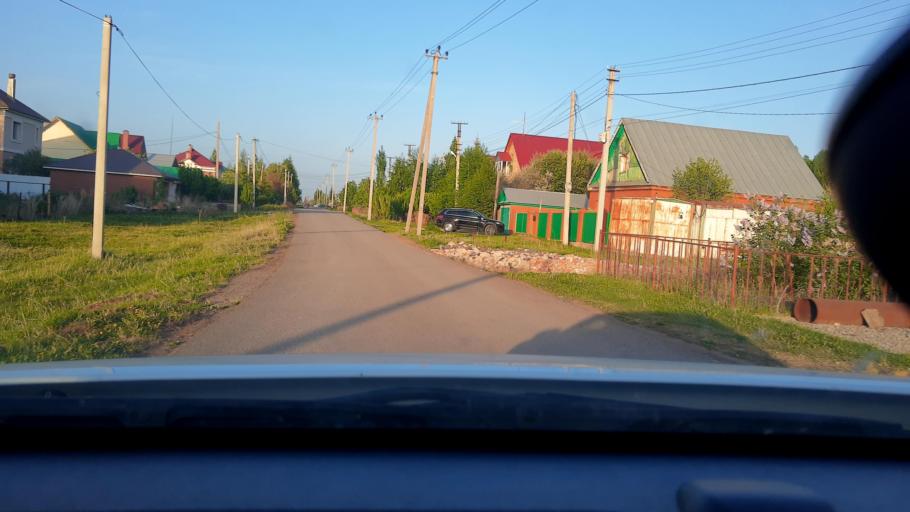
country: RU
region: Bashkortostan
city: Avdon
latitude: 54.4921
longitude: 55.8669
